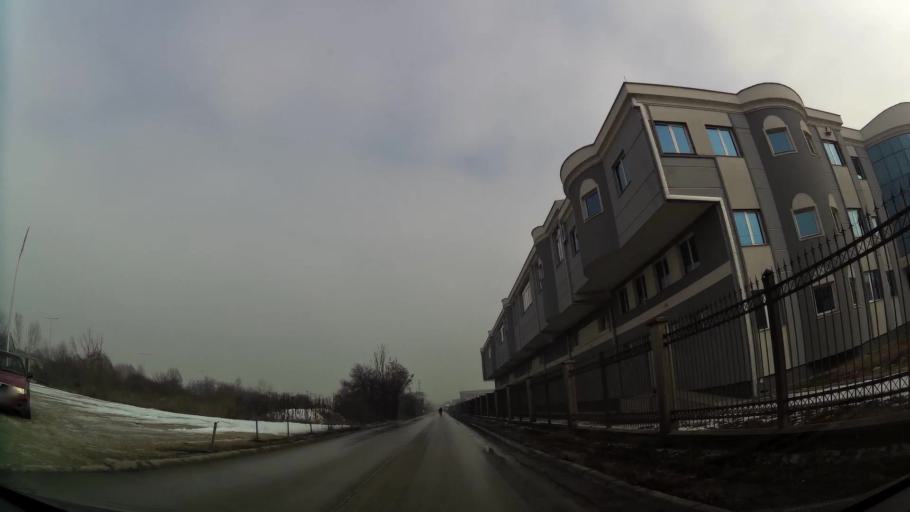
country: MK
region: Ilinden
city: Jurumleri
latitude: 41.9949
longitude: 21.5480
